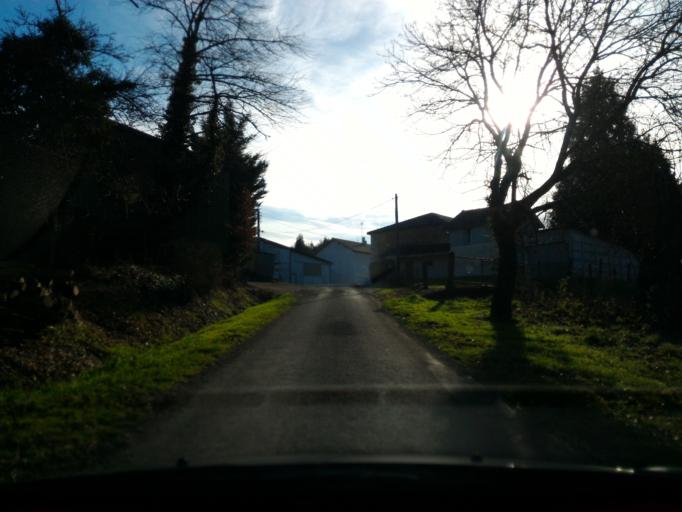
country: FR
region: Poitou-Charentes
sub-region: Departement de la Charente
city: Etagnac
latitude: 45.9339
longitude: 0.7727
